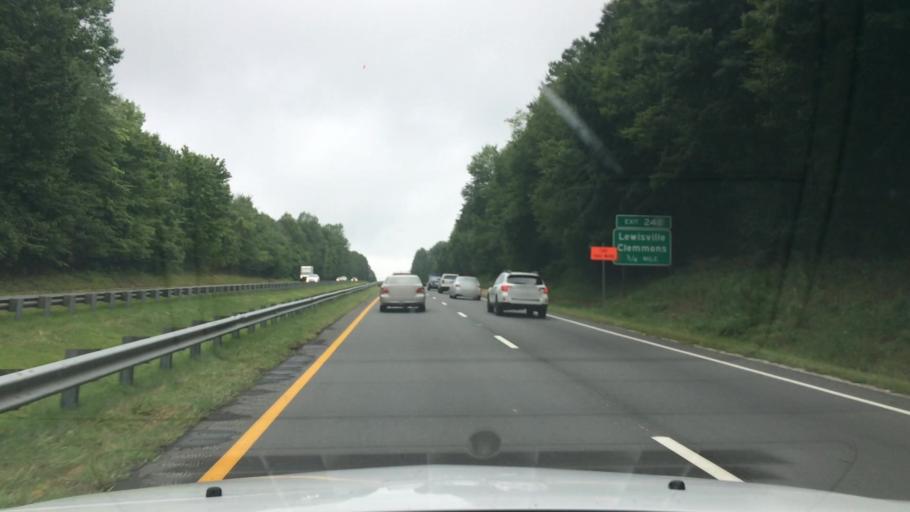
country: US
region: North Carolina
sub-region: Forsyth County
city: Lewisville
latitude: 36.0747
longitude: -80.3717
